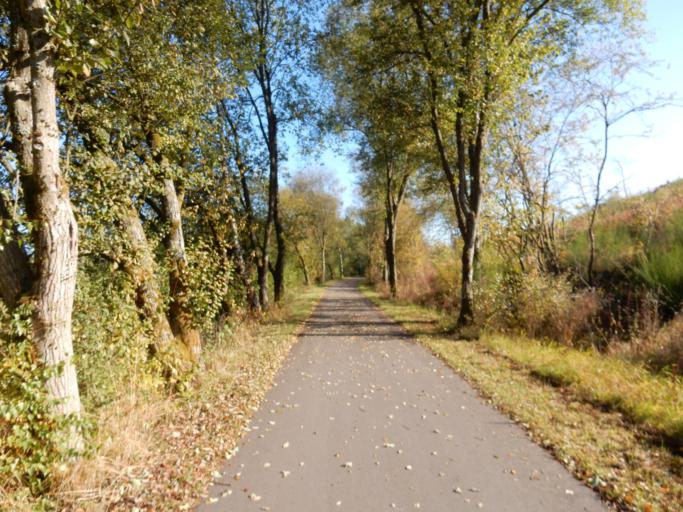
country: LU
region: Diekirch
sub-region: Canton de Clervaux
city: Troisvierges
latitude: 50.1306
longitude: 5.9954
